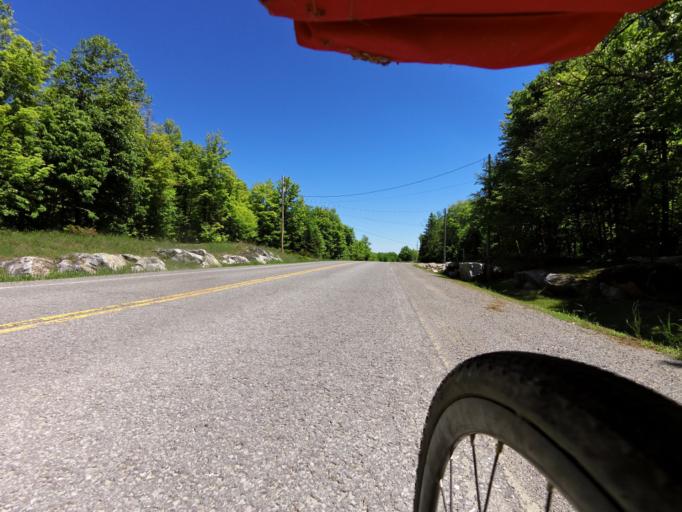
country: CA
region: Ontario
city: Carleton Place
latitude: 45.1840
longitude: -76.3731
